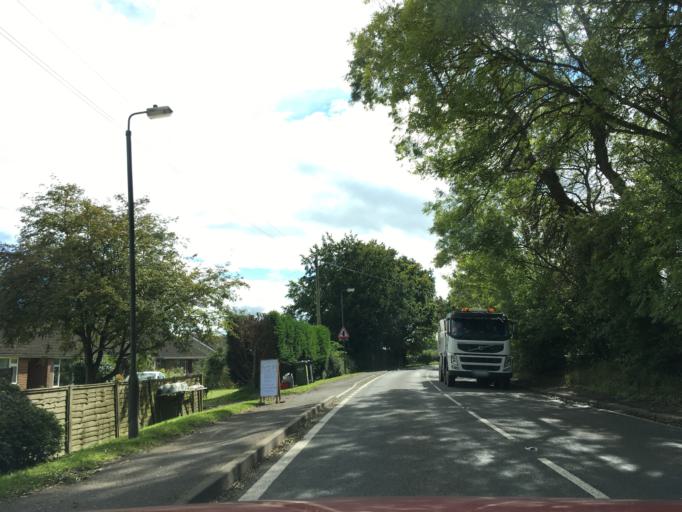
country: GB
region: England
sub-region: South Gloucestershire
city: Yate
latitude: 51.5689
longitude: -2.4464
